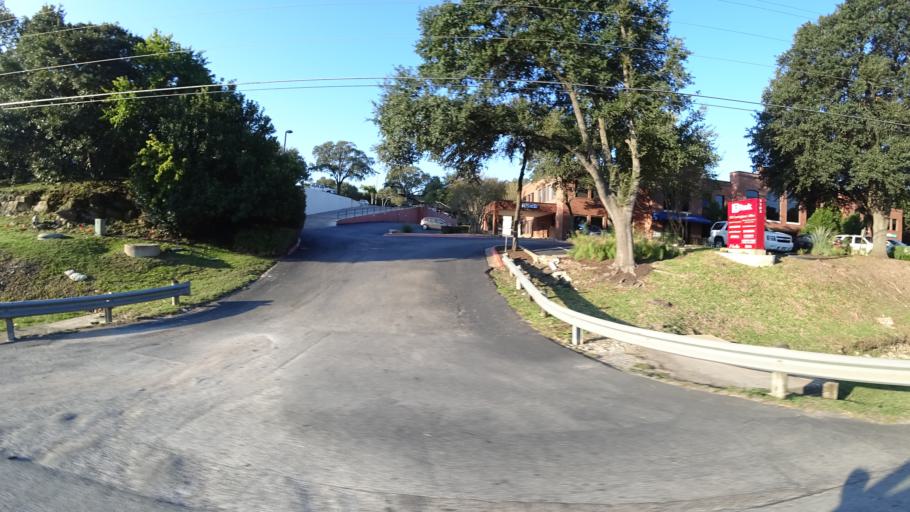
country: US
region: Texas
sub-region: Travis County
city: Rollingwood
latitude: 30.2725
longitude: -97.7977
